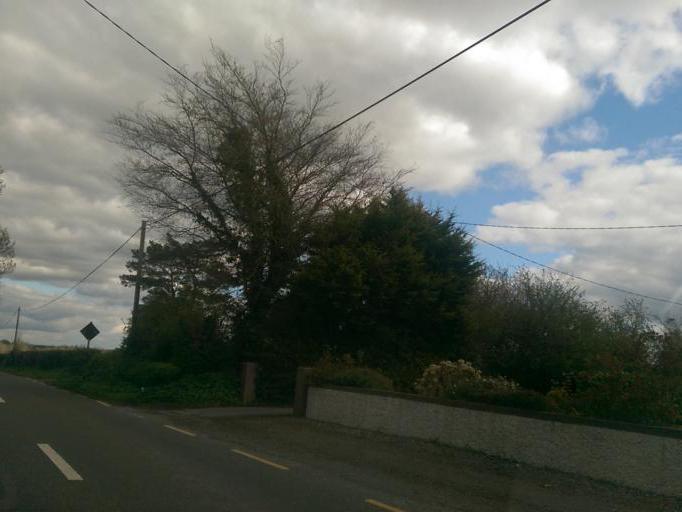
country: IE
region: Connaught
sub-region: County Galway
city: Ballinasloe
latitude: 53.4231
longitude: -8.3989
